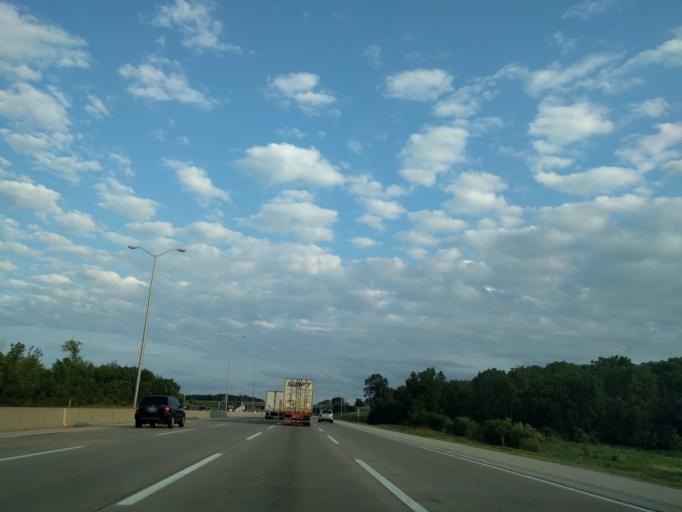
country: US
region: Illinois
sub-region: Lake County
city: Gurnee
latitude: 42.3485
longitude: -87.9264
